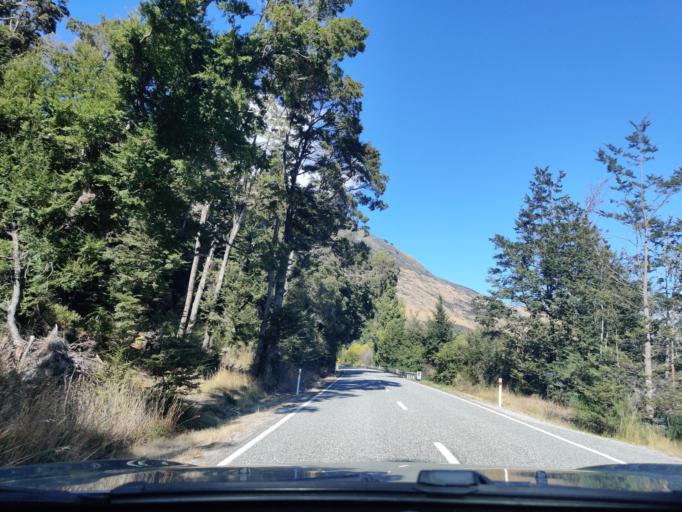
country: NZ
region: Otago
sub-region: Queenstown-Lakes District
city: Queenstown
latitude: -44.9978
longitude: 168.4361
